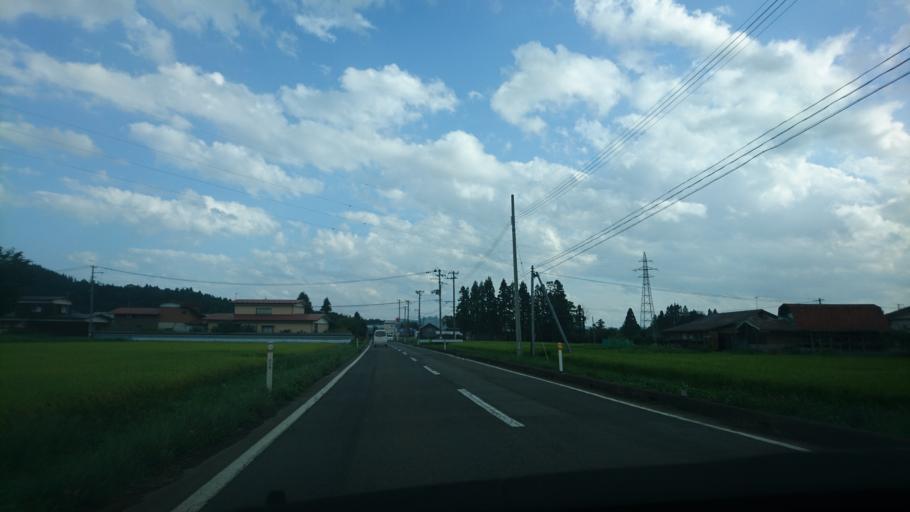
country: JP
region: Iwate
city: Hanamaki
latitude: 39.3411
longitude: 141.1520
